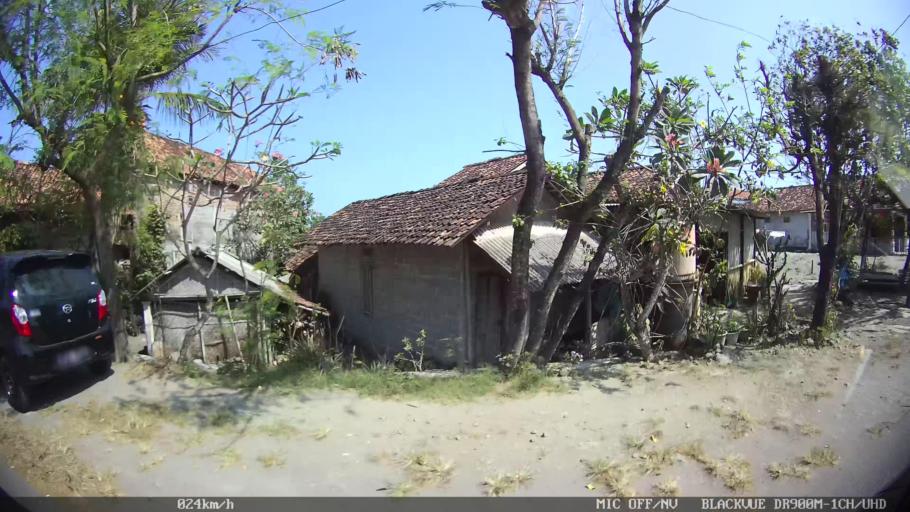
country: ID
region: Daerah Istimewa Yogyakarta
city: Pundong
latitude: -8.0196
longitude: 110.3236
